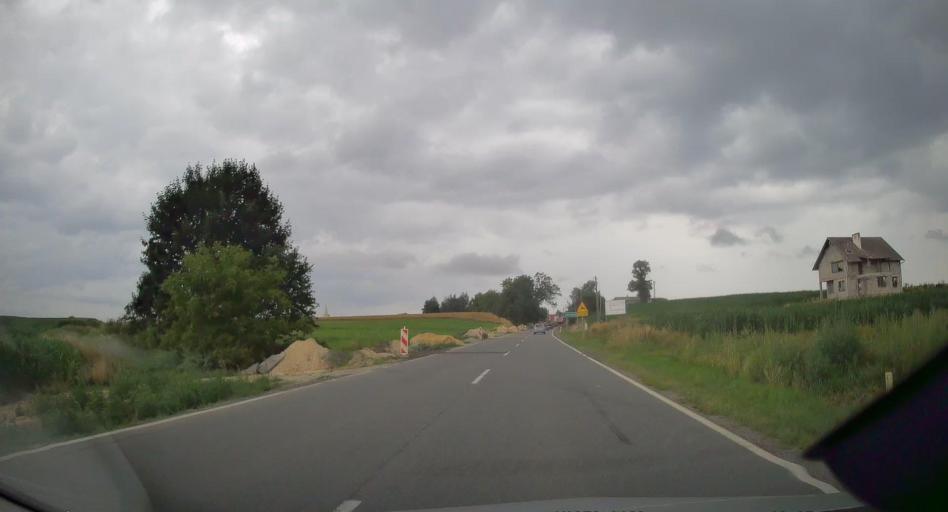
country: PL
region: Opole Voivodeship
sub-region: Powiat nyski
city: Nysa
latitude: 50.4234
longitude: 17.4397
